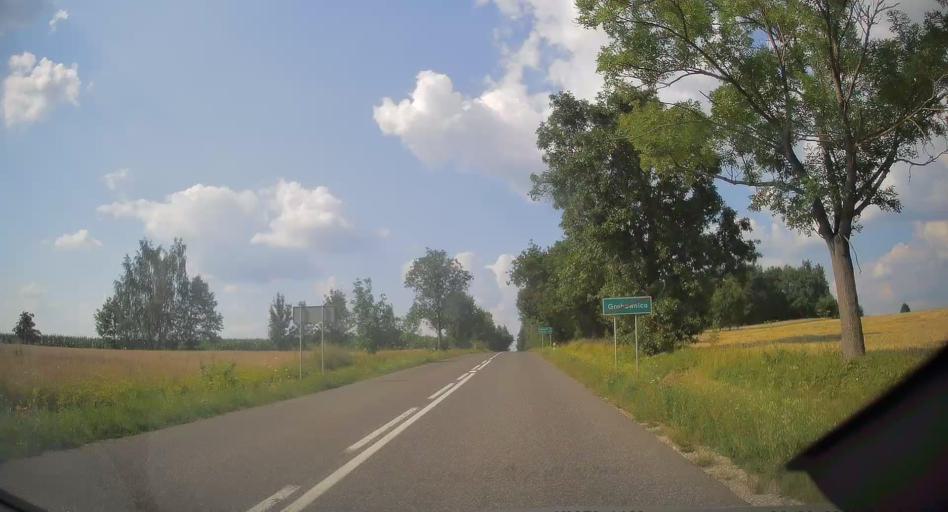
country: PL
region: Swietokrzyskie
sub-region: Powiat kielecki
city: Lopuszno
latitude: 50.9243
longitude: 20.2402
